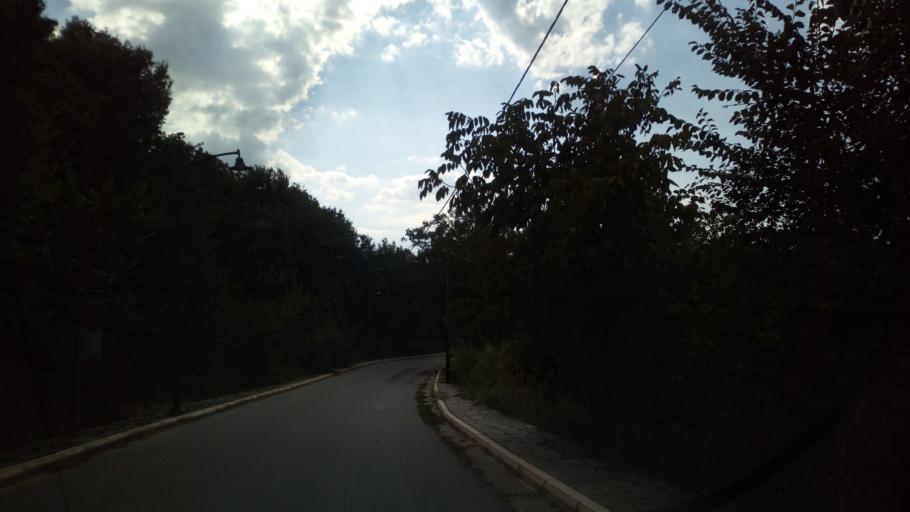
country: GR
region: Central Macedonia
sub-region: Nomos Chalkidikis
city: Galatista
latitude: 40.5142
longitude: 23.3479
